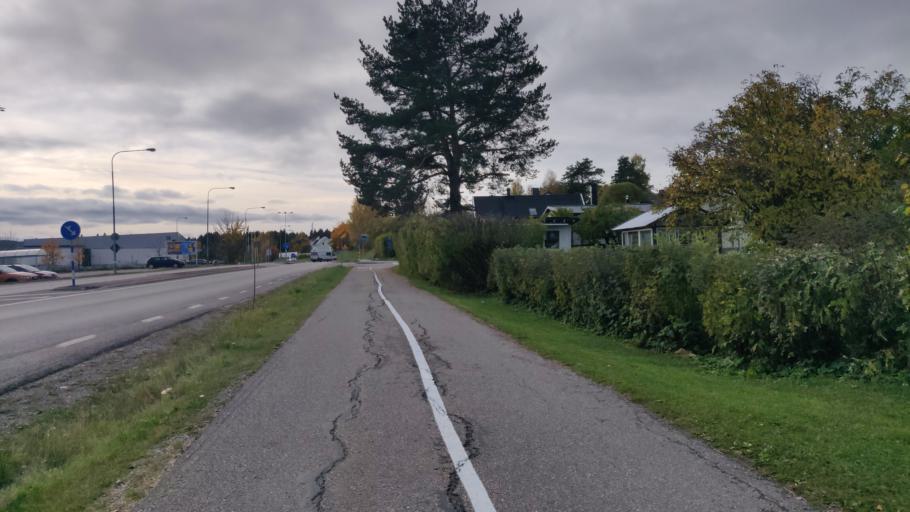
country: SE
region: Vaesternorrland
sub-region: Sundsvalls Kommun
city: Sundsvall
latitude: 62.4140
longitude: 17.3382
